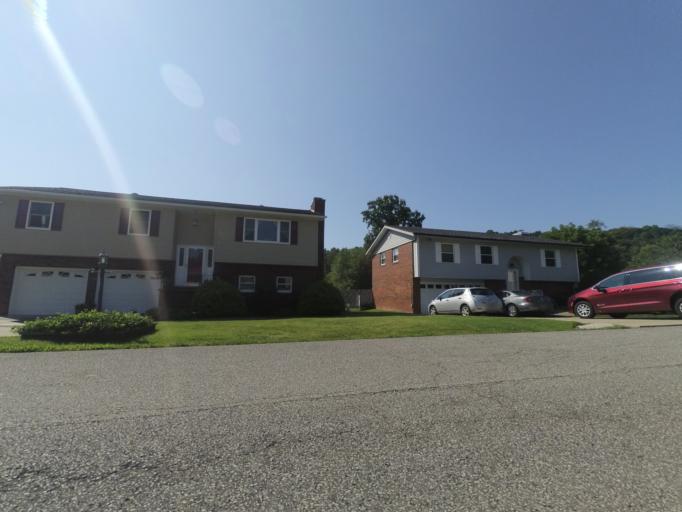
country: US
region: West Virginia
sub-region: Cabell County
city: Huntington
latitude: 38.4422
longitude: -82.4374
